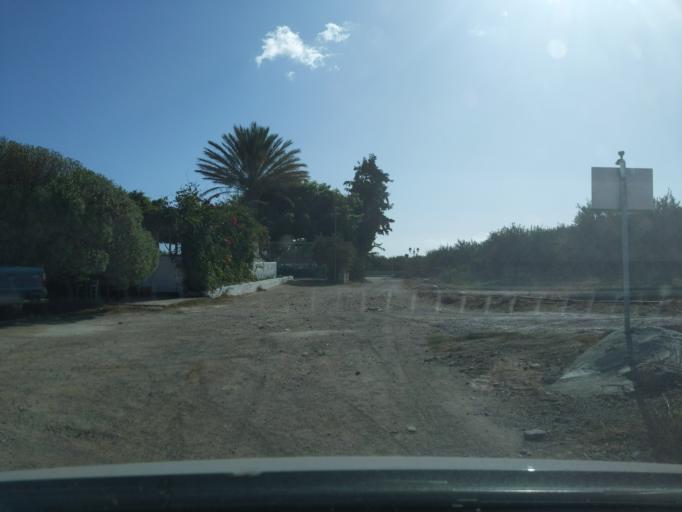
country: GR
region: Crete
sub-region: Nomos Lasithiou
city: Palekastro
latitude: 35.2122
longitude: 26.2667
